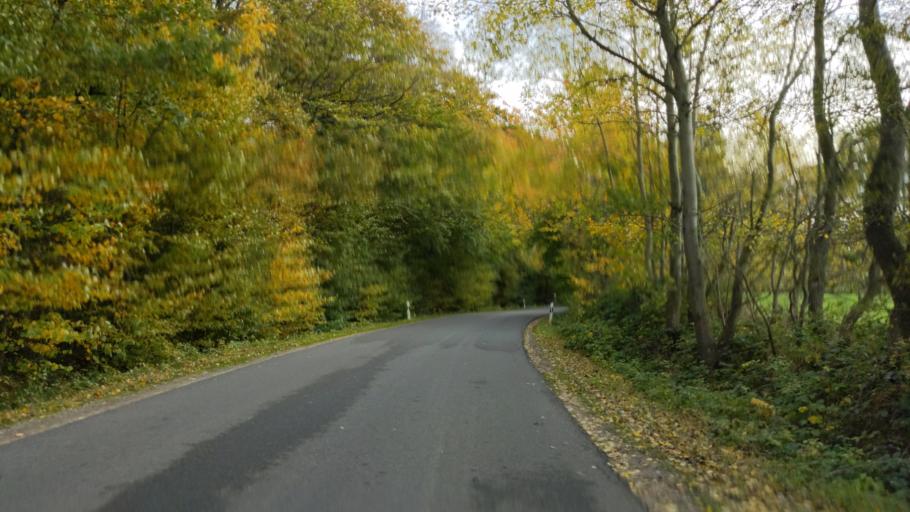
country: DE
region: Schleswig-Holstein
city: Susel
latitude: 54.0511
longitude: 10.7182
